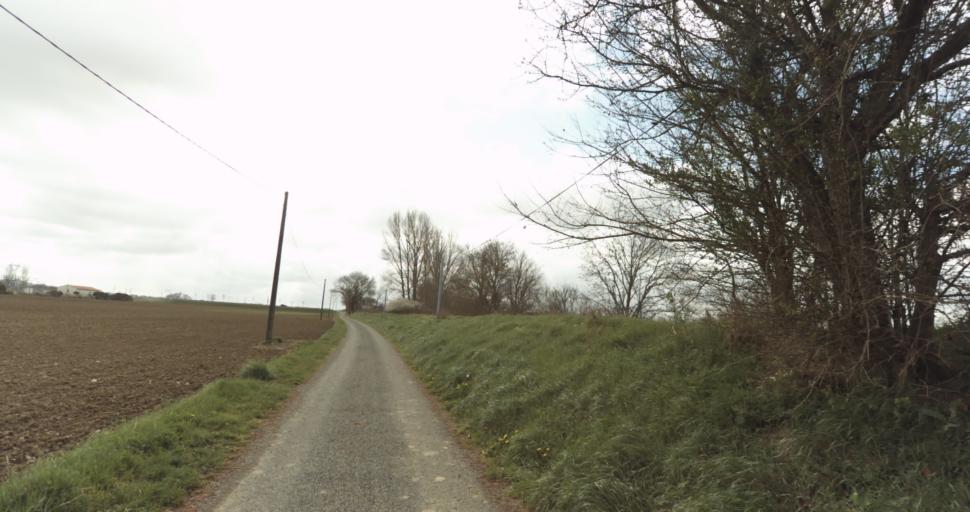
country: FR
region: Midi-Pyrenees
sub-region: Departement de la Haute-Garonne
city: Miremont
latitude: 43.3485
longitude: 1.4422
